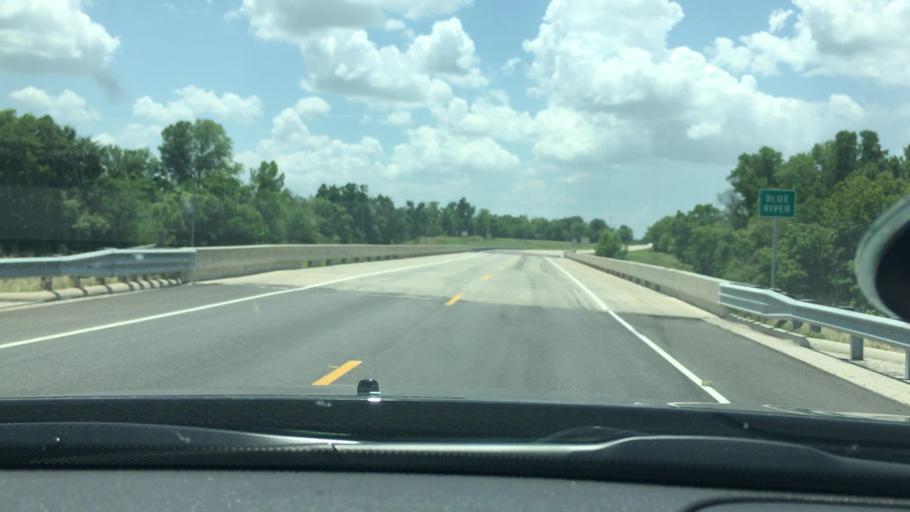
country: US
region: Oklahoma
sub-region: Johnston County
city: Tishomingo
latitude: 34.4551
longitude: -96.6358
